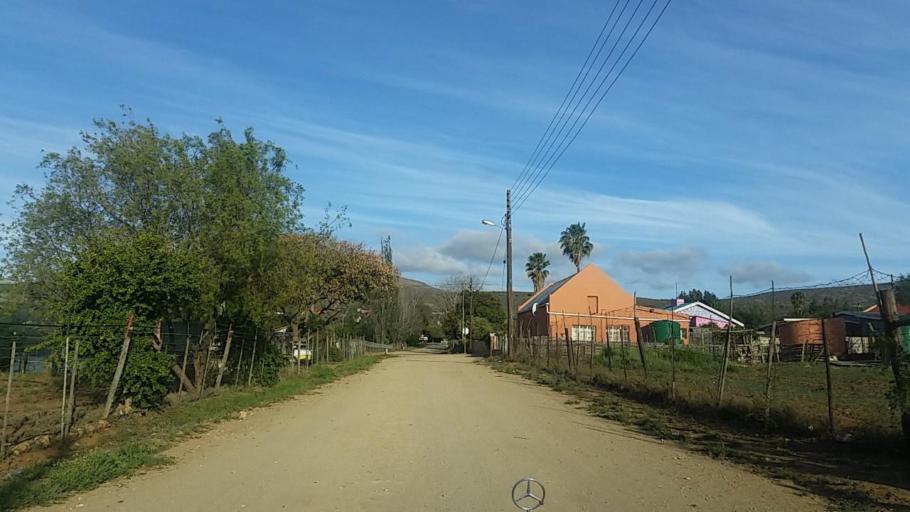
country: ZA
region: Western Cape
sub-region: Eden District Municipality
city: Knysna
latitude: -33.6580
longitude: 23.1206
